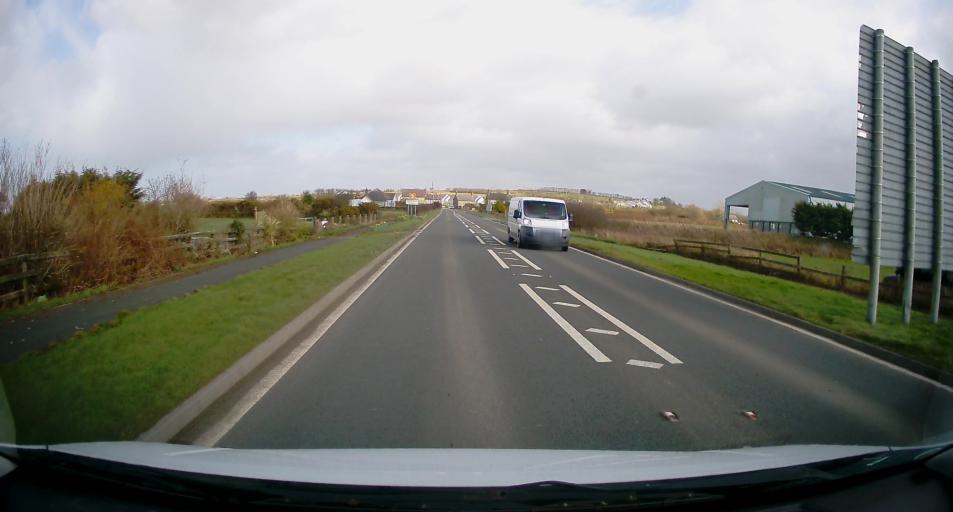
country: GB
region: Wales
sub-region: County of Ceredigion
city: Aberporth
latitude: 52.1151
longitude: -4.5106
